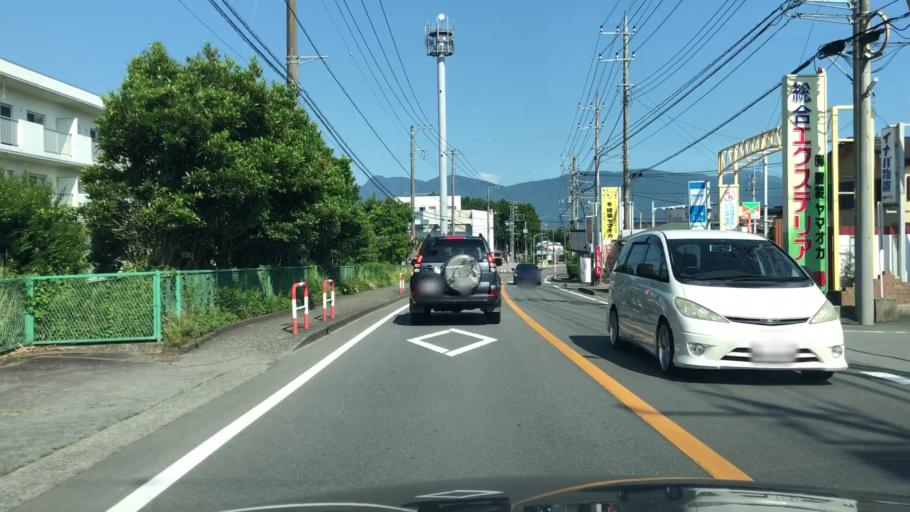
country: JP
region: Shizuoka
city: Gotemba
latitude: 35.3134
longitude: 138.9006
